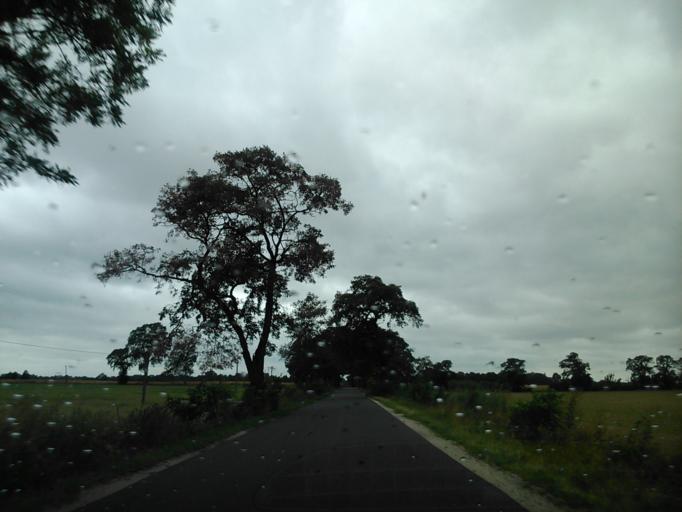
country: PL
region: Kujawsko-Pomorskie
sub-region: Powiat inowroclawski
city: Kruszwica
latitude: 52.5902
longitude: 18.3960
